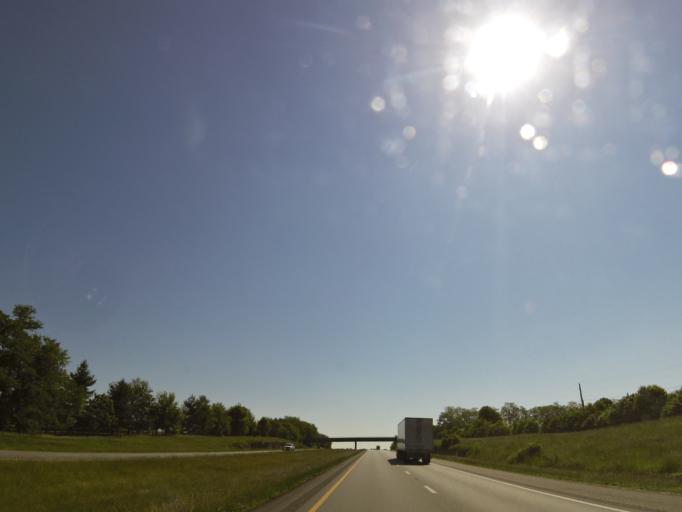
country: US
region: Kentucky
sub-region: Woodford County
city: Midway
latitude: 38.1616
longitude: -84.6409
